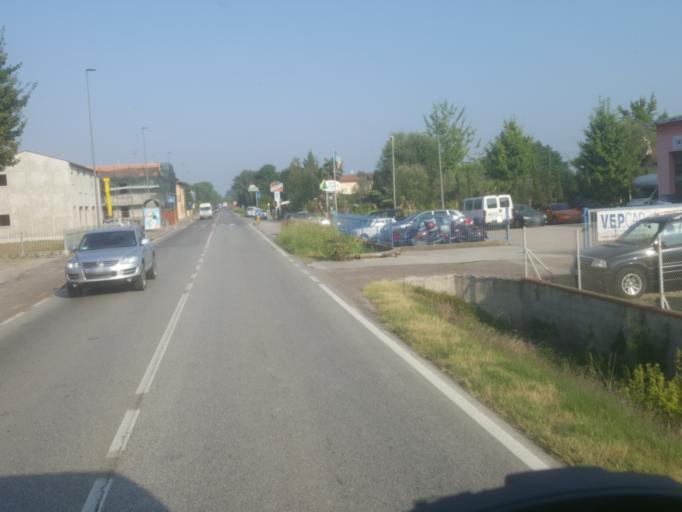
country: IT
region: Emilia-Romagna
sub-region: Provincia di Ravenna
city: Mezzano
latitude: 44.4587
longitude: 12.1008
